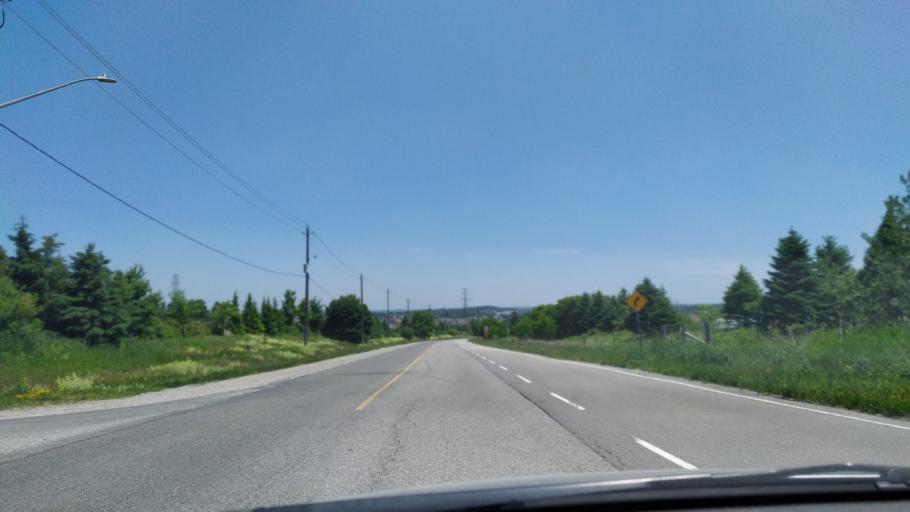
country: CA
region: Ontario
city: Kitchener
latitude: 43.3990
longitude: -80.5223
